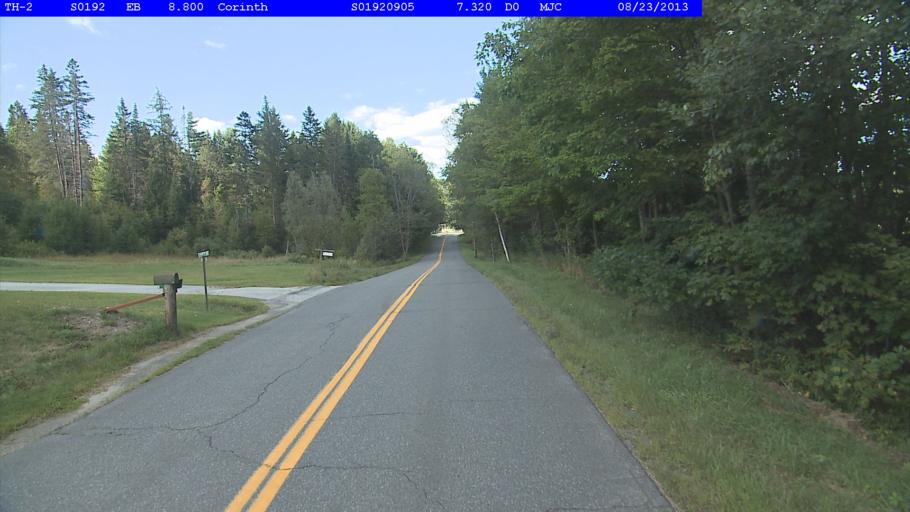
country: US
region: New Hampshire
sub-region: Grafton County
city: Orford
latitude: 44.0135
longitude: -72.2343
